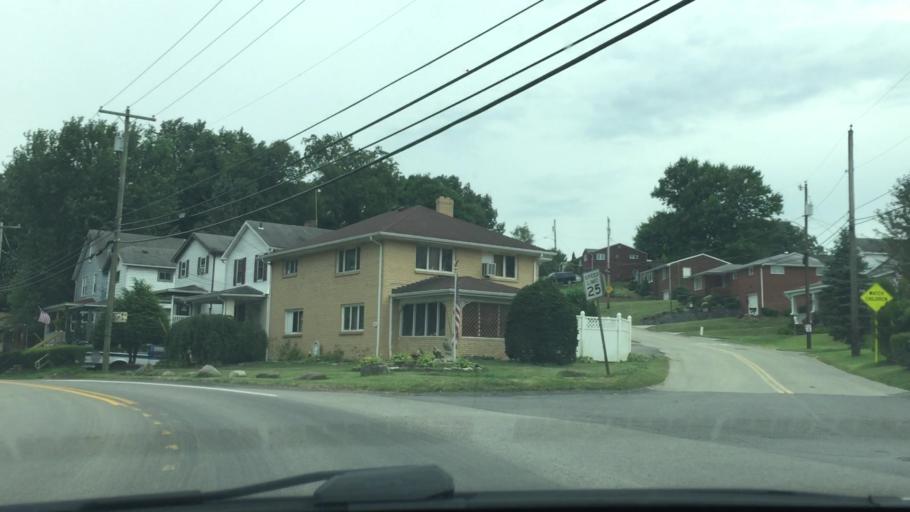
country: US
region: Pennsylvania
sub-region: Allegheny County
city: Bridgeville
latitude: 40.3655
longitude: -80.1153
